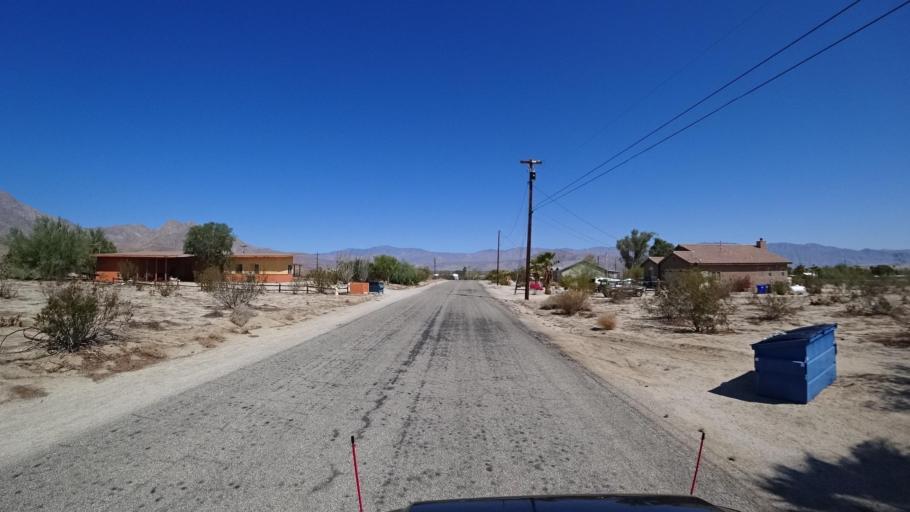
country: US
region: California
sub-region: San Diego County
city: Borrego Springs
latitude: 33.2326
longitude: -116.3723
